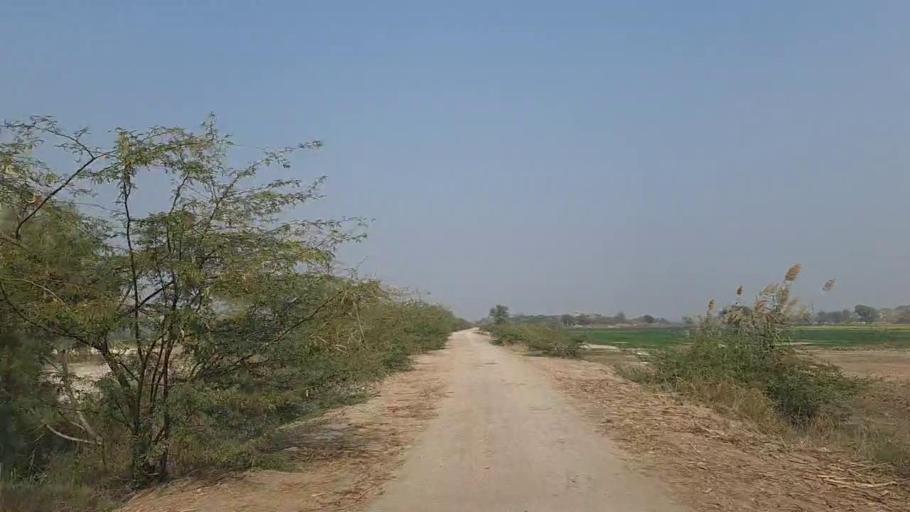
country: PK
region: Sindh
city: Daur
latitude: 26.4348
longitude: 68.4426
